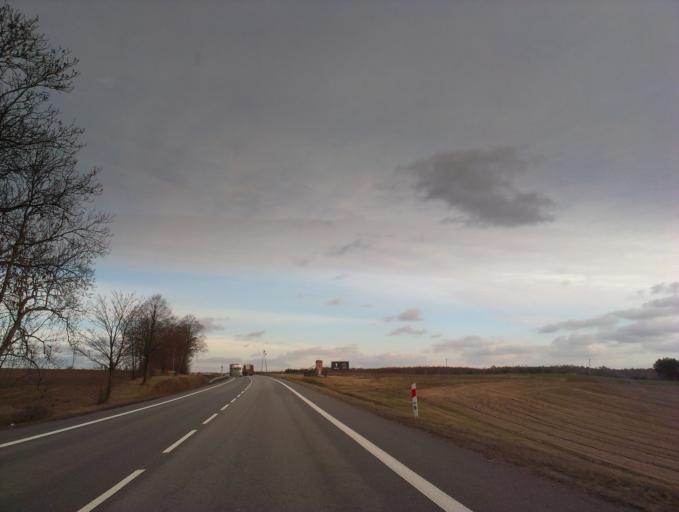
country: PL
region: Kujawsko-Pomorskie
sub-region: Powiat lipnowski
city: Skepe
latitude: 52.8572
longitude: 19.2943
